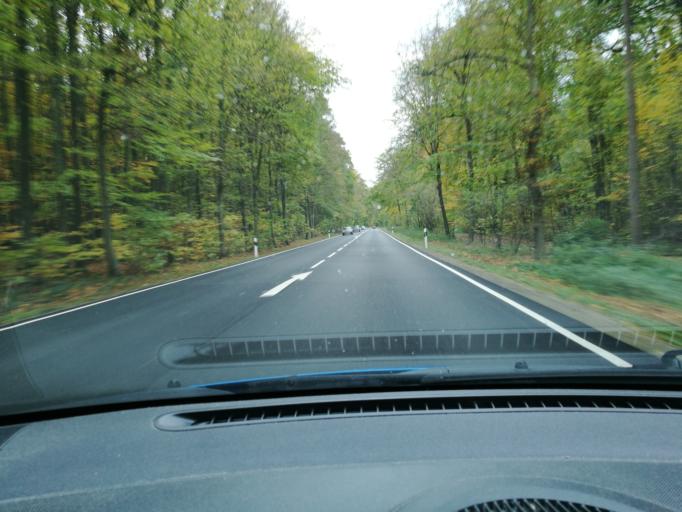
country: DE
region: Schleswig-Holstein
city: Fredeburg
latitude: 53.6695
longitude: 10.7213
